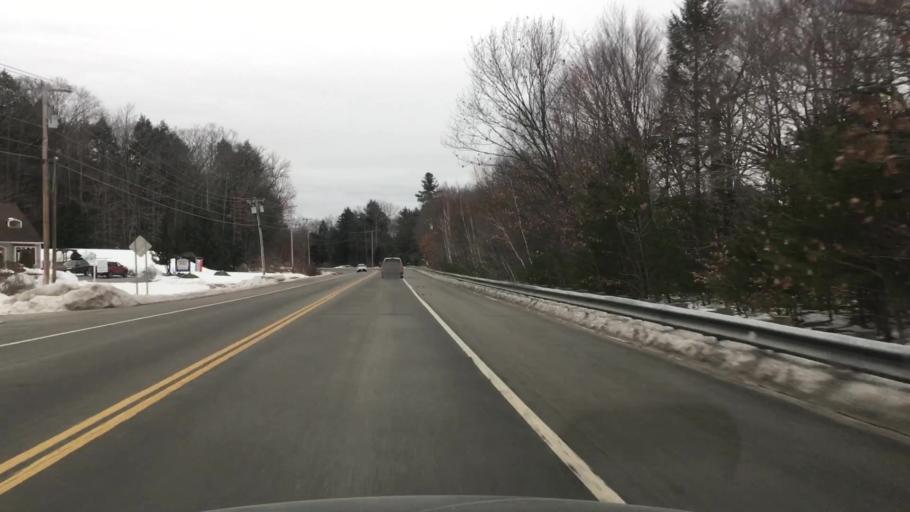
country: US
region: New Hampshire
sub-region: Merrimack County
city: Sutton
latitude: 43.2797
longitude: -71.9746
